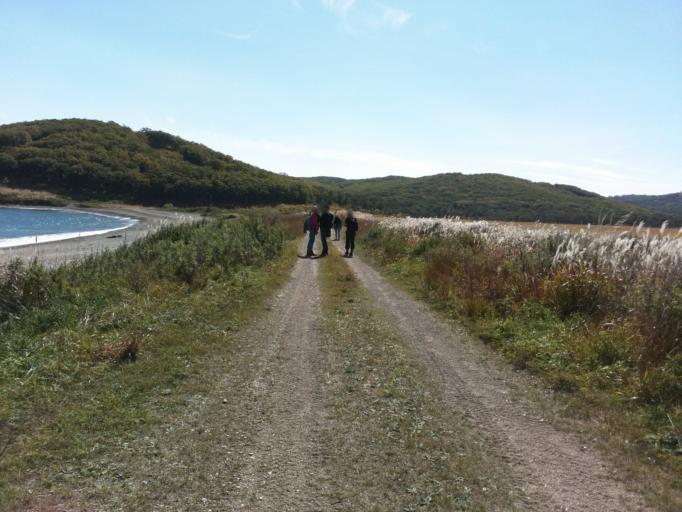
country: RU
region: Primorskiy
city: Zarubino
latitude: 42.7022
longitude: 131.2360
